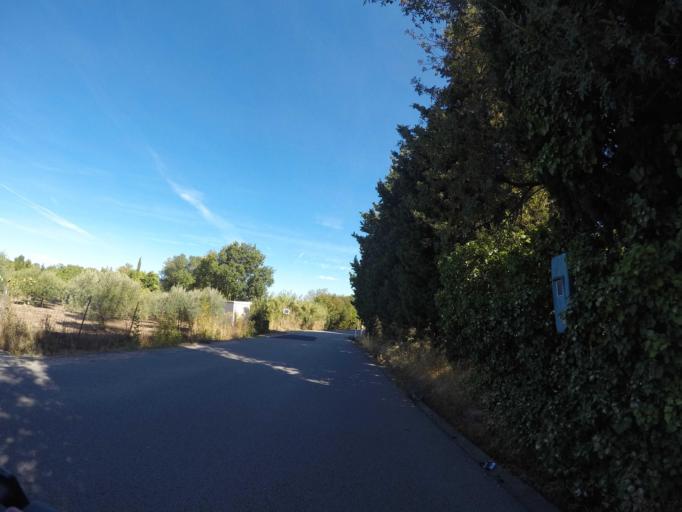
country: FR
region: Languedoc-Roussillon
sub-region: Departement des Pyrenees-Orientales
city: Le Soler
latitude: 42.6757
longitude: 2.7896
